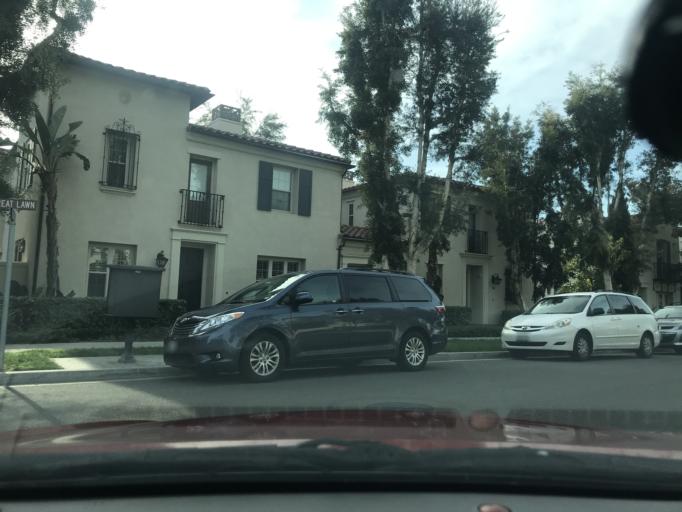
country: US
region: California
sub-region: Orange County
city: Irvine
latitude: 33.6983
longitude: -117.7546
